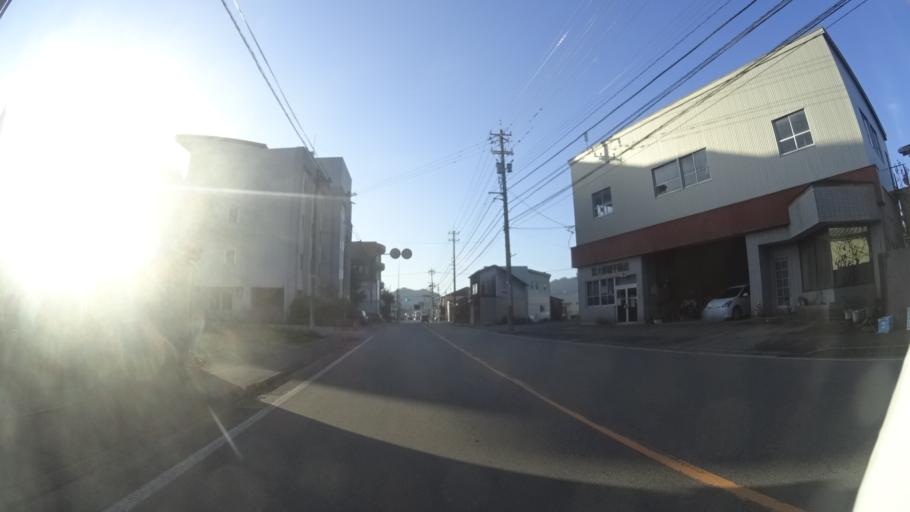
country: JP
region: Fukui
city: Ono
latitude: 35.9905
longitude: 136.4900
